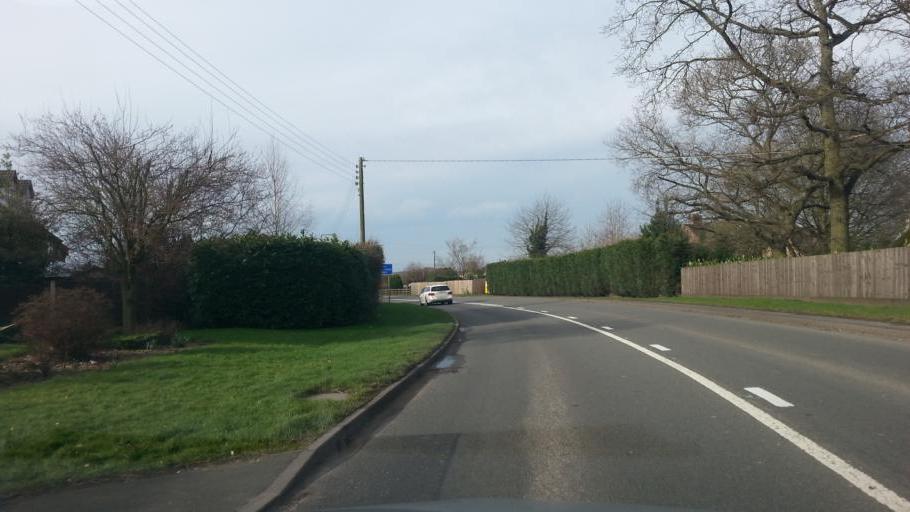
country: GB
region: England
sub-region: Staffordshire
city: Colwich
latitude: 52.8395
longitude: -2.0318
